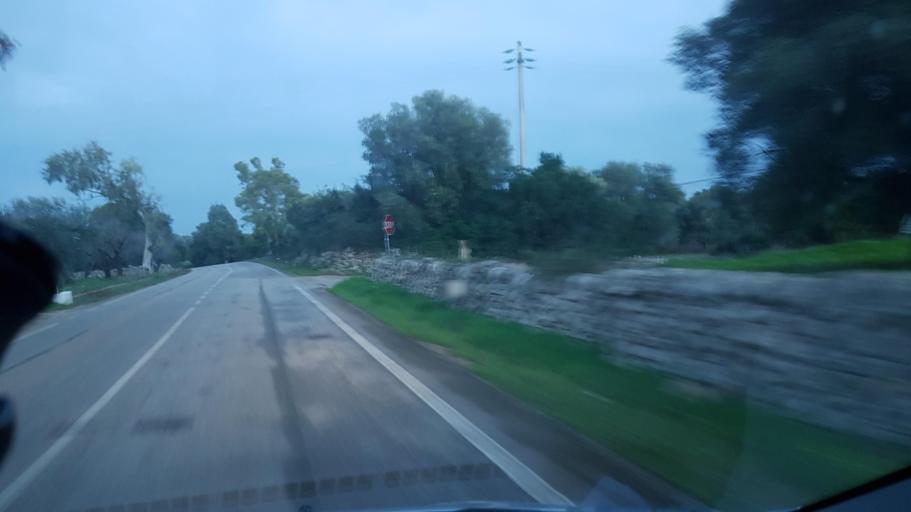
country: IT
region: Apulia
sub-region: Provincia di Brindisi
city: San Michele Salentino
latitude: 40.6410
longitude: 17.5863
